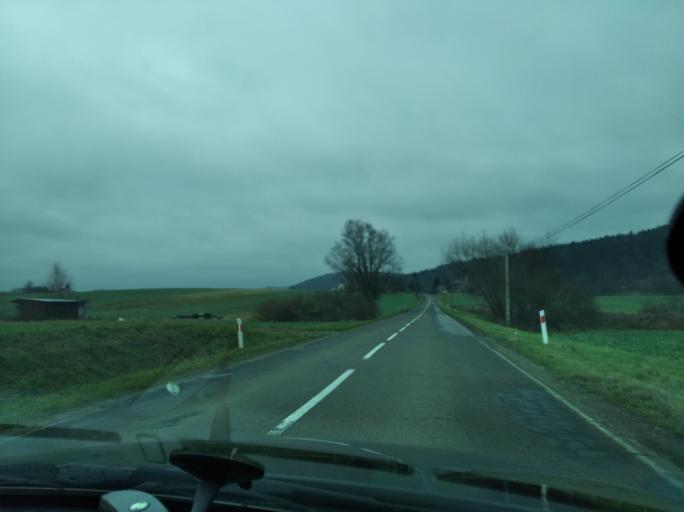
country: PL
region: Subcarpathian Voivodeship
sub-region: Powiat rzeszowski
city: Dynow
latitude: 49.8527
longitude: 22.2479
